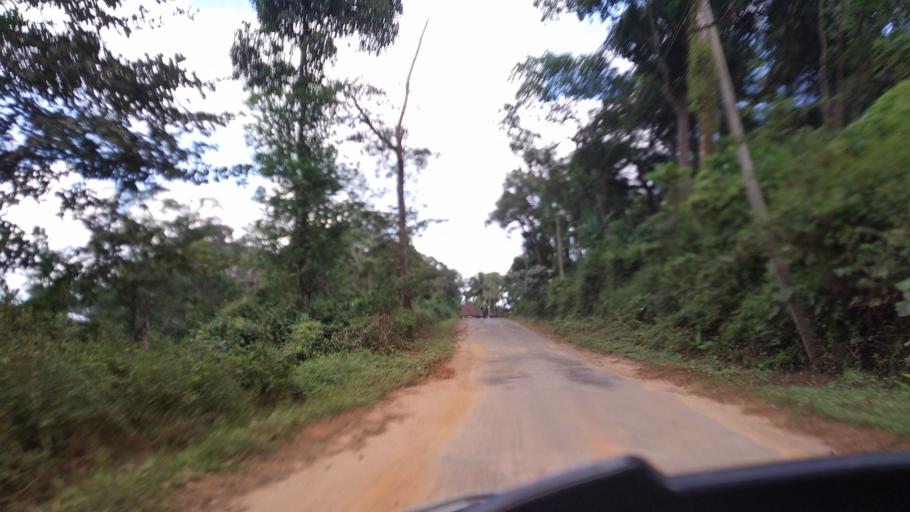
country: IN
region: Karnataka
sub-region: Kodagu
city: Ponnampet
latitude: 12.0370
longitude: 75.9070
